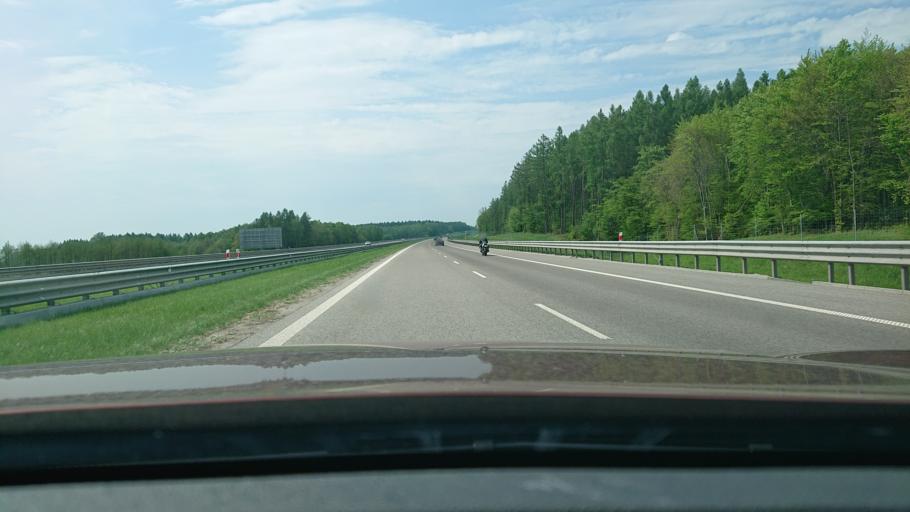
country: PL
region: Subcarpathian Voivodeship
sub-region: Powiat jaroslawski
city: Pawlosiow
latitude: 49.9856
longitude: 22.6180
